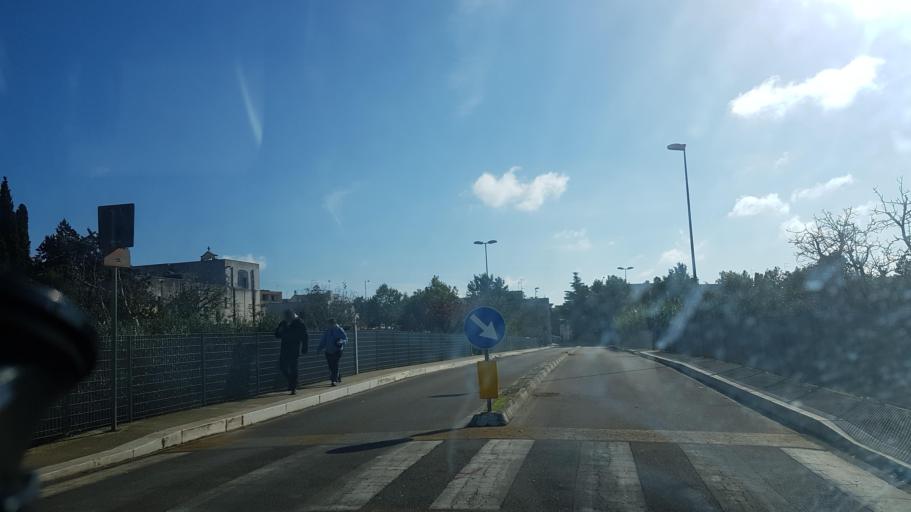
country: IT
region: Apulia
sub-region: Provincia di Brindisi
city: San Vito dei Normanni
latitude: 40.6588
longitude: 17.6999
